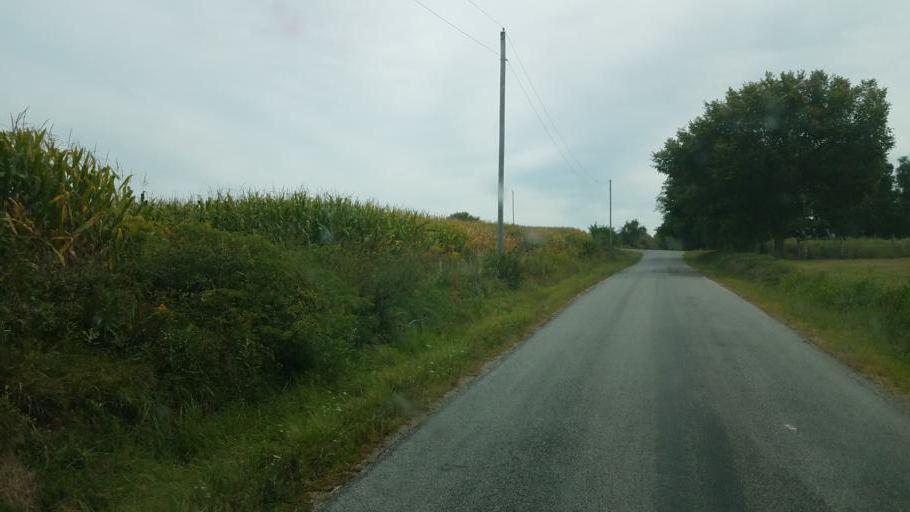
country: US
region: Ohio
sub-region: Knox County
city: Centerburg
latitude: 40.3482
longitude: -82.7127
